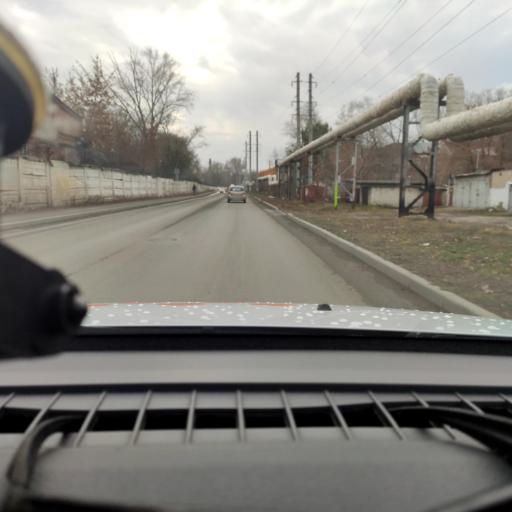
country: RU
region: Samara
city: Chapayevsk
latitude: 52.9730
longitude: 49.7110
